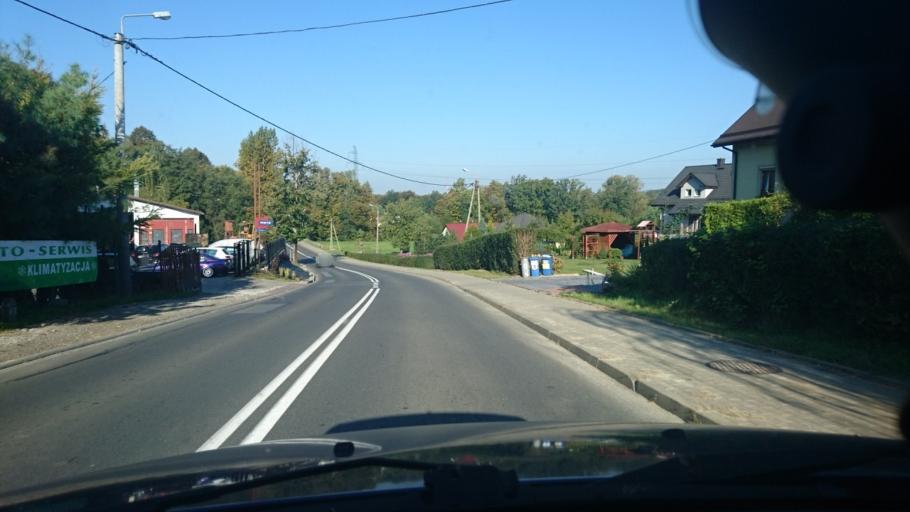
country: PL
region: Silesian Voivodeship
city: Janowice
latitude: 49.8504
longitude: 19.0826
